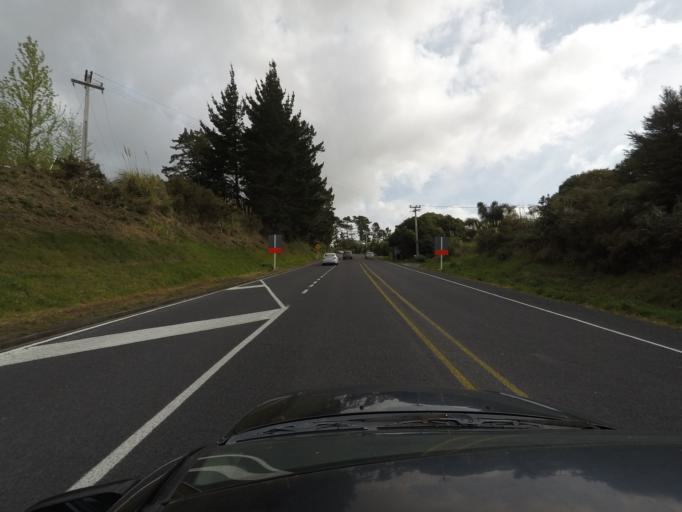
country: NZ
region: Auckland
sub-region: Auckland
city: Pakuranga
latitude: -36.9259
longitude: 174.9360
